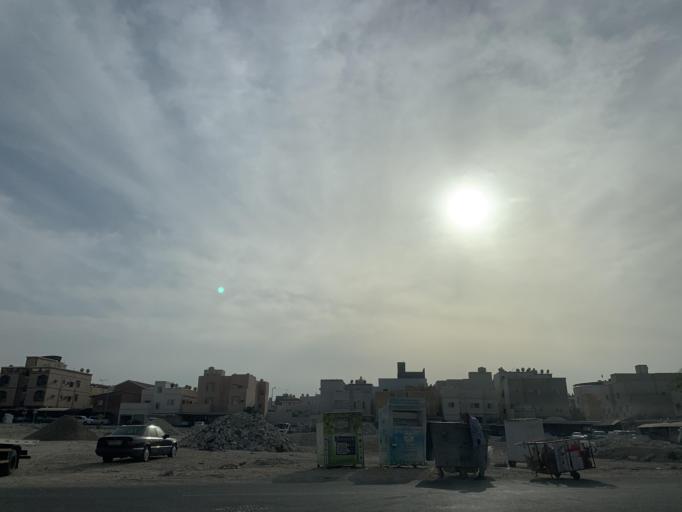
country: BH
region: Northern
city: Ar Rifa'
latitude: 26.1238
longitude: 50.5828
